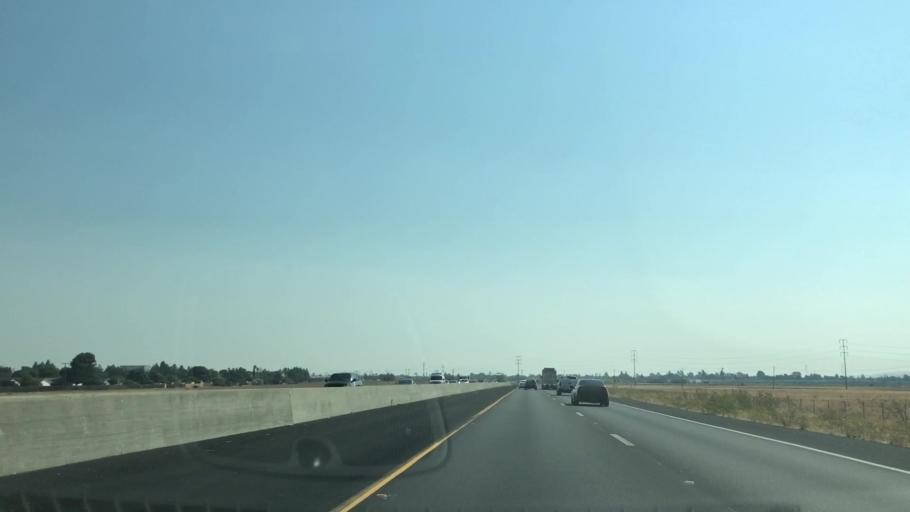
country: US
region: California
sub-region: Solano County
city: Suisun
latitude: 38.2405
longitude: -122.0602
